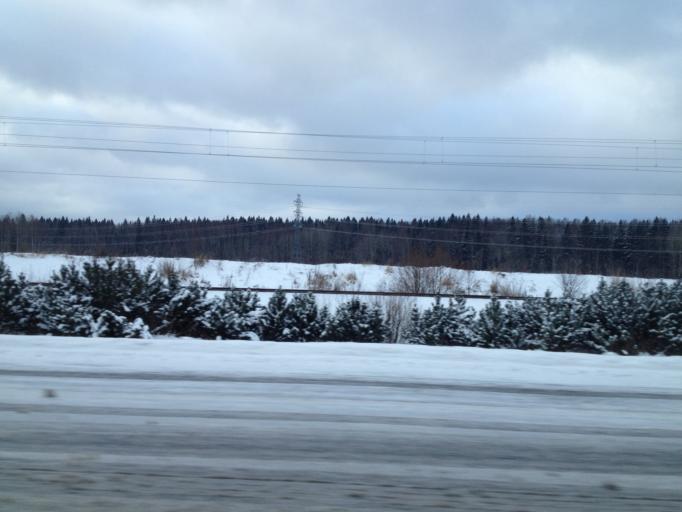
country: FI
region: Uusimaa
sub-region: Helsinki
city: Vantaa
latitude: 60.2423
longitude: 25.1512
